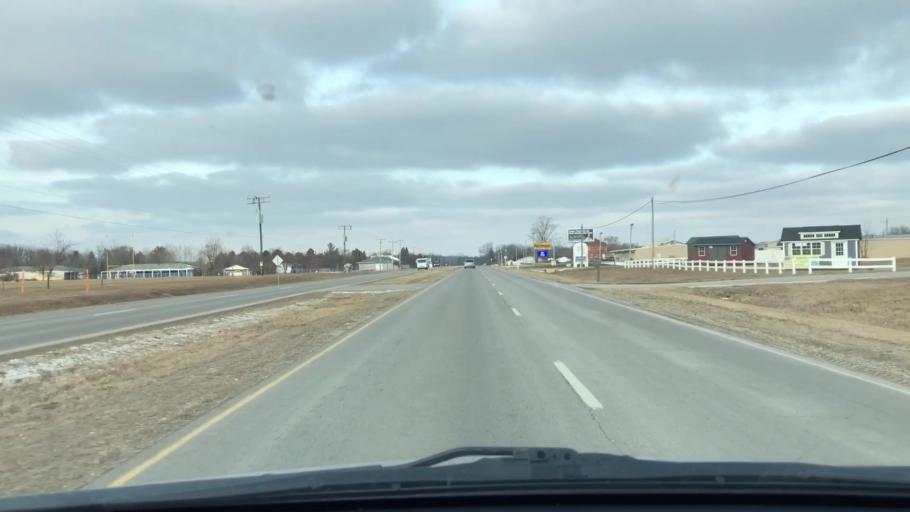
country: US
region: Indiana
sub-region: Steuben County
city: Angola
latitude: 41.6729
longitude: -85.0286
